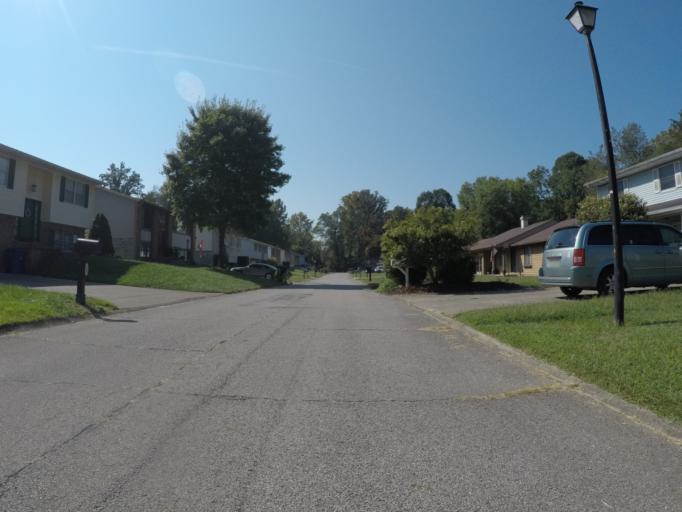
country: US
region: West Virginia
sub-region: Cabell County
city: Barboursville
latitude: 38.3681
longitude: -82.2759
